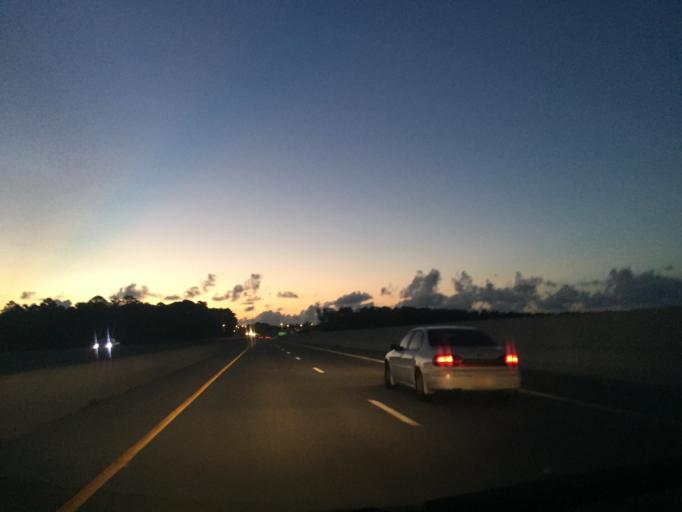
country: US
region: Georgia
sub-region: Chatham County
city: Montgomery
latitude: 31.9750
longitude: -81.1158
